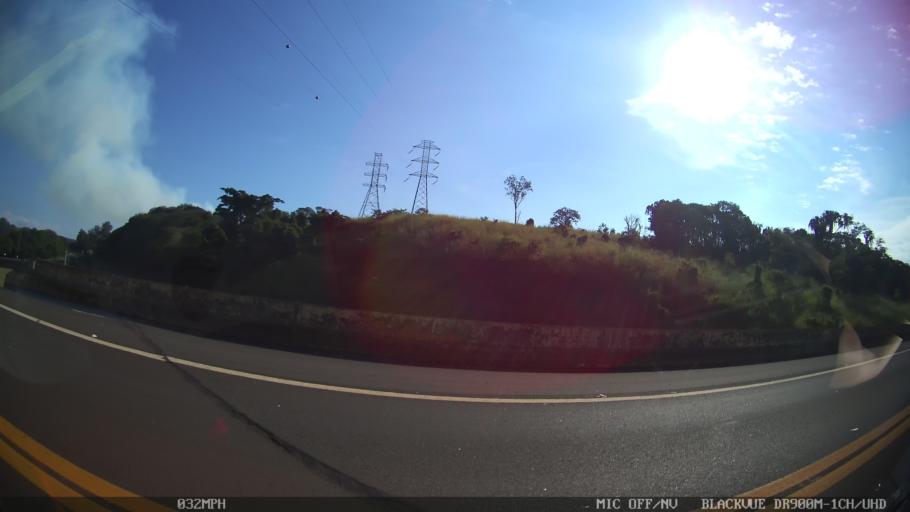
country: BR
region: Sao Paulo
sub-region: Piracicaba
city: Piracicaba
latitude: -22.6873
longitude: -47.5826
